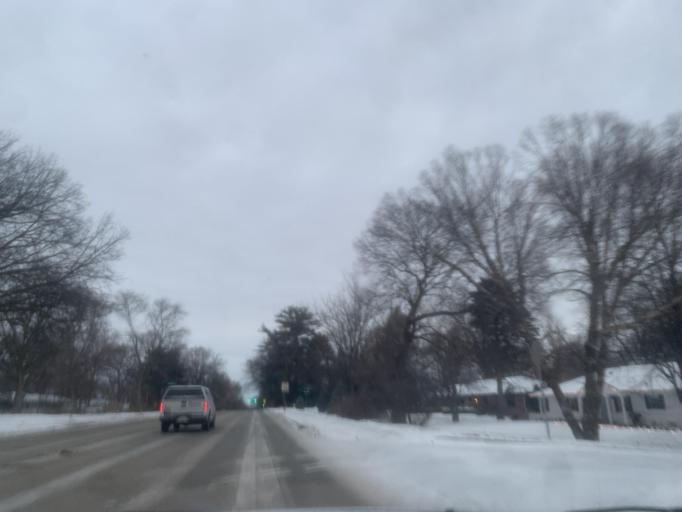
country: US
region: Nebraska
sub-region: Douglas County
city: Ralston
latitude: 41.2534
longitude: -96.0526
